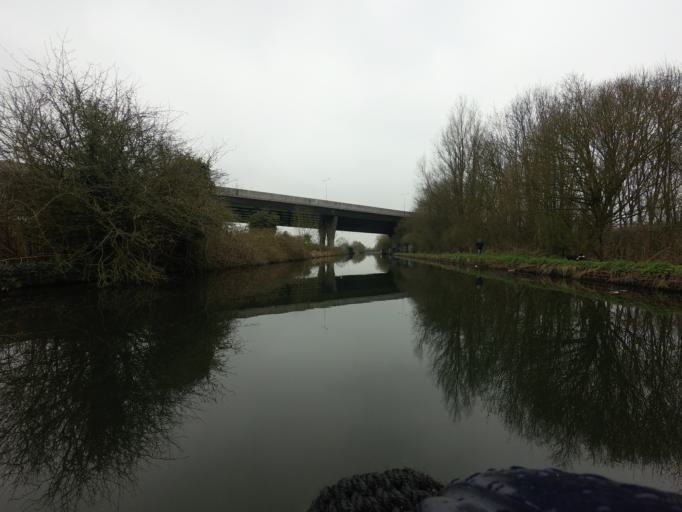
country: GB
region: England
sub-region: Hertfordshire
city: Kings Langley
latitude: 51.7040
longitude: -0.4413
